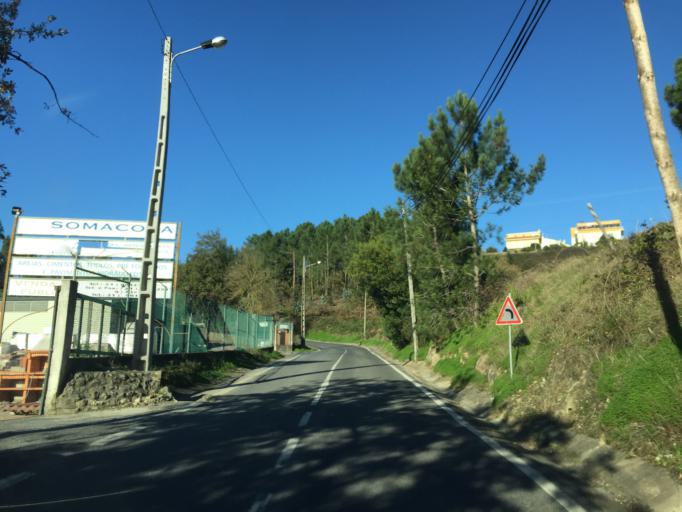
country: PT
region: Lisbon
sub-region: Odivelas
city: Canecas
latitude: 38.8189
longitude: -9.2306
